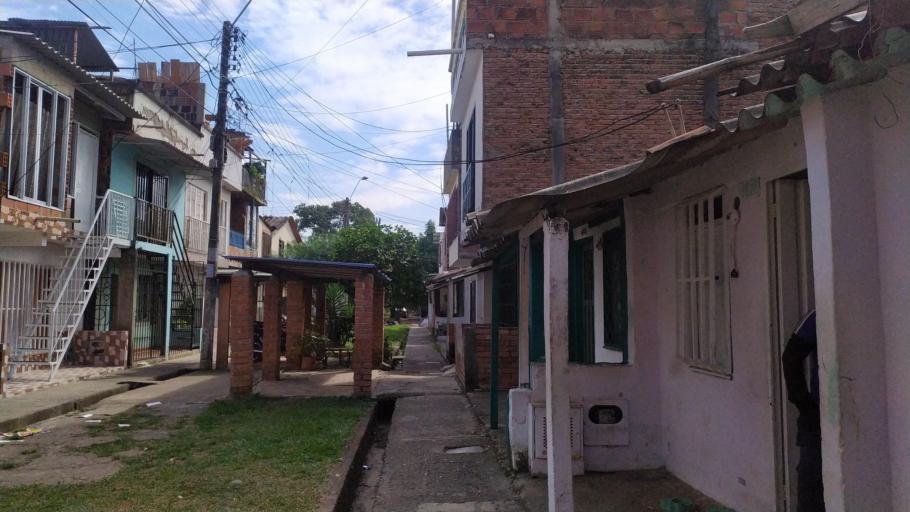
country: CO
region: Valle del Cauca
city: Jamundi
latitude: 3.2548
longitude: -76.5442
